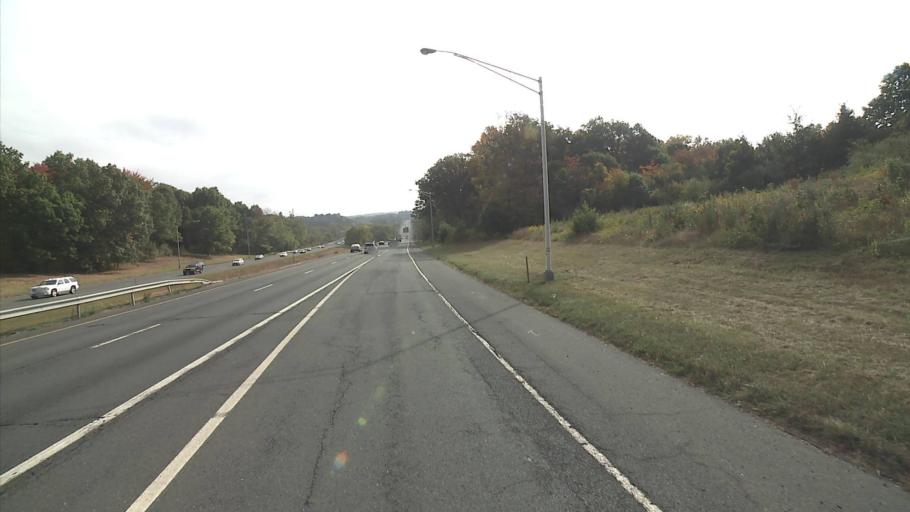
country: US
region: Connecticut
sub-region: Fairfield County
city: Newtown
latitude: 41.4166
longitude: -73.2874
